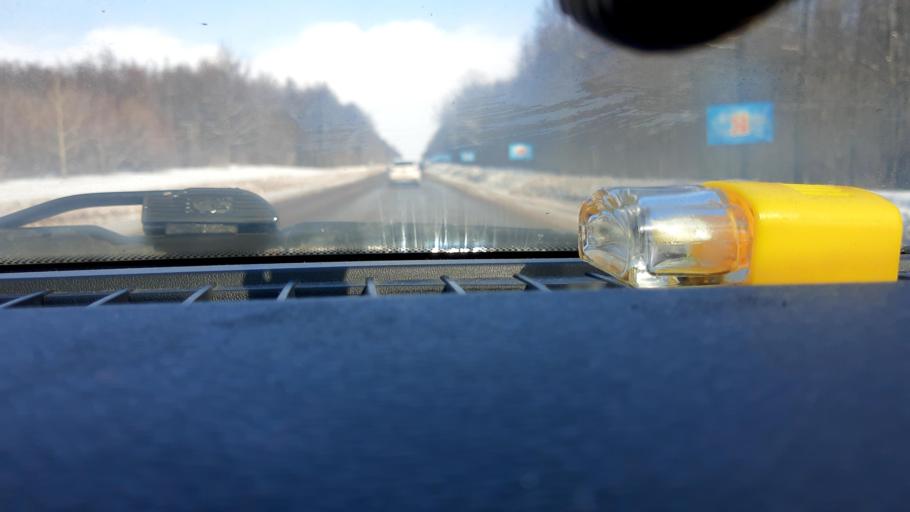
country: RU
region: Bashkortostan
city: Iglino
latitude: 54.7661
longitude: 56.4173
